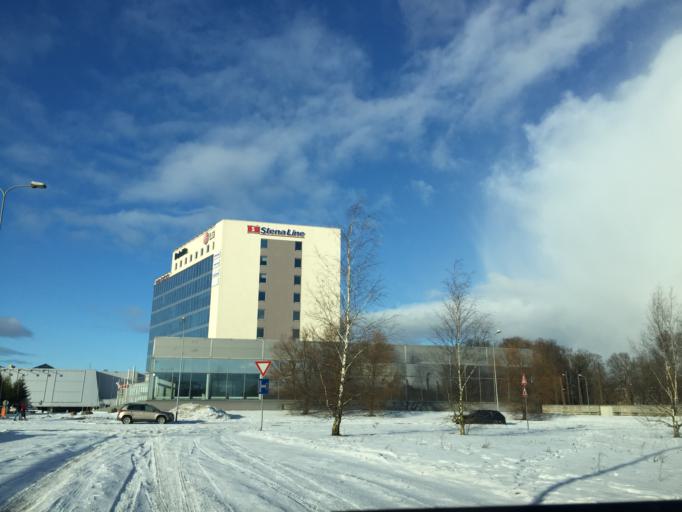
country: LV
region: Riga
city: Riga
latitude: 56.9307
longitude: 24.1559
